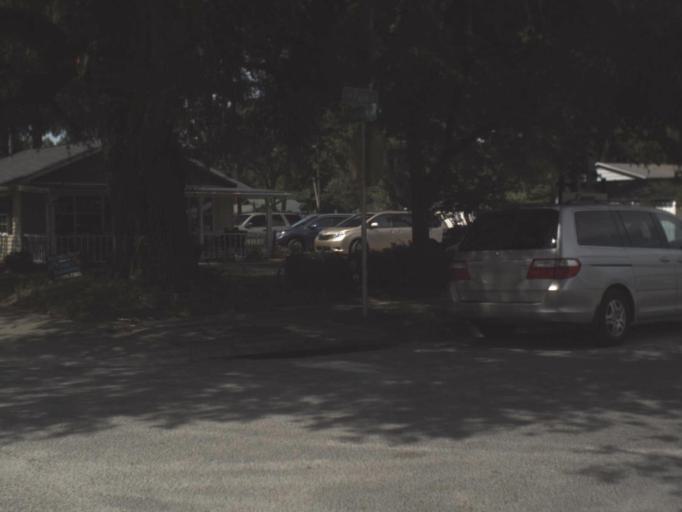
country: US
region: Florida
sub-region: Lafayette County
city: Mayo
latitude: 30.0525
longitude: -83.1753
